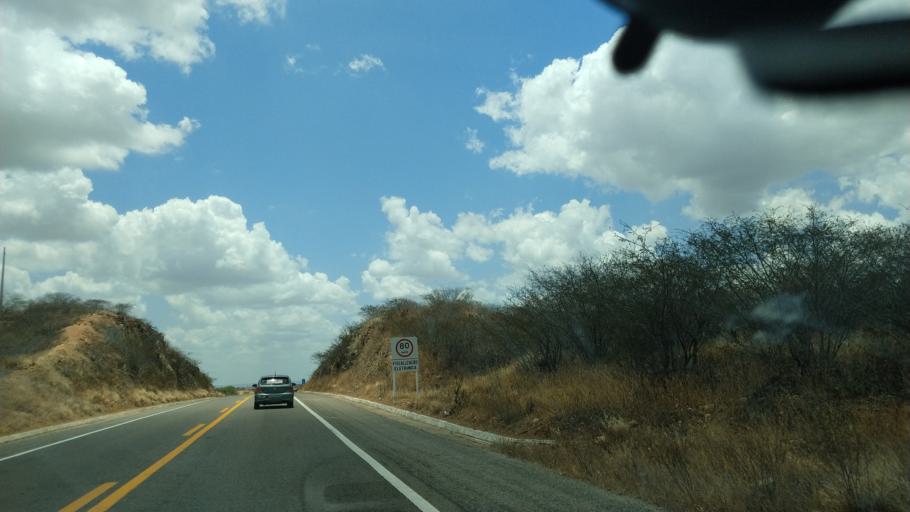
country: BR
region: Rio Grande do Norte
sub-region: Cerro Cora
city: Cerro Cora
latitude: -6.2102
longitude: -36.3058
